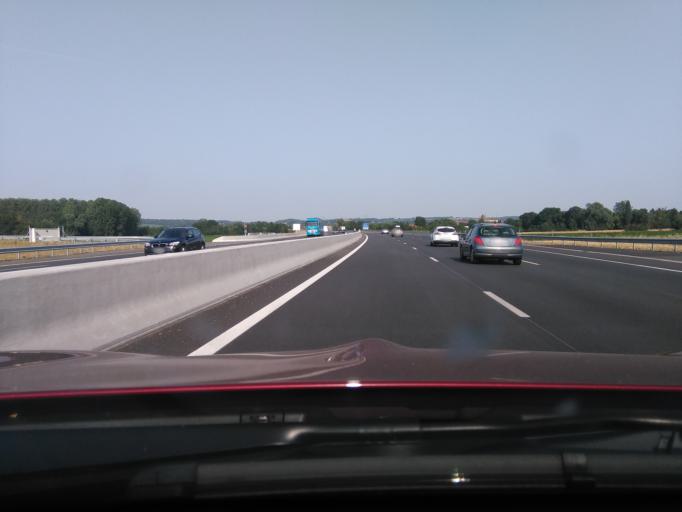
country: FR
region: Rhone-Alpes
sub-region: Departement du Rhone
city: Quincieux
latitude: 45.9187
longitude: 4.7755
